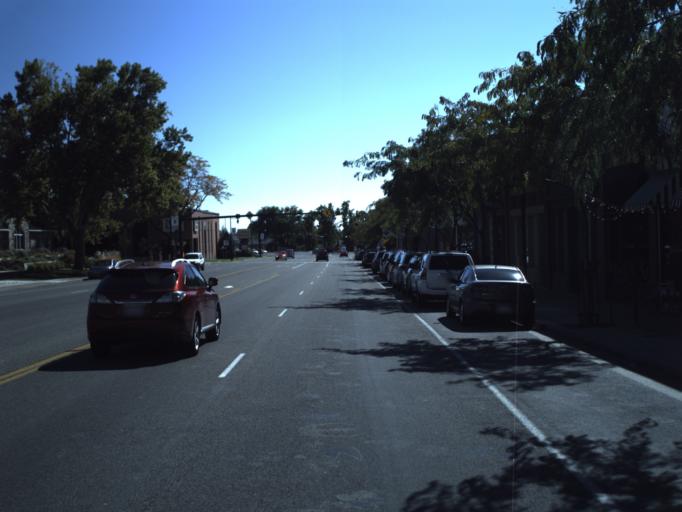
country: US
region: Utah
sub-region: Davis County
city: Kaysville
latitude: 41.0362
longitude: -111.9387
